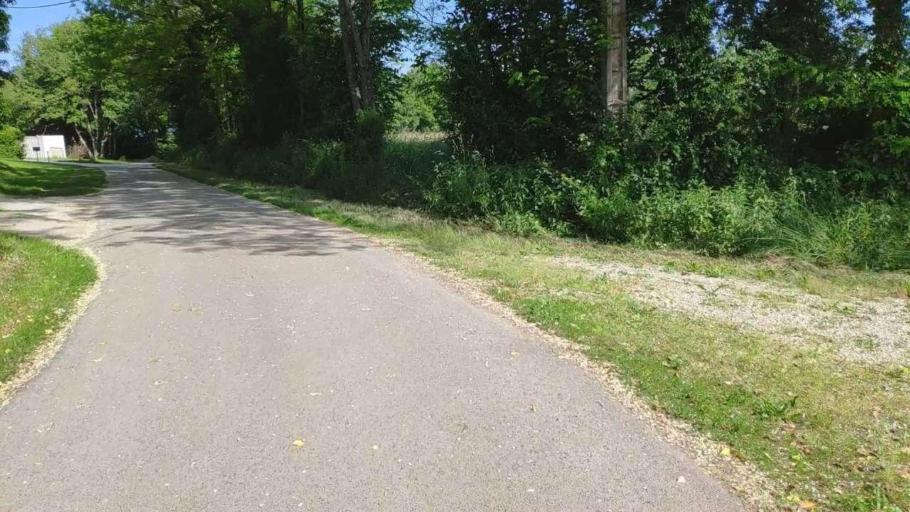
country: FR
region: Franche-Comte
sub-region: Departement du Jura
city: Bletterans
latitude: 46.7144
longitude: 5.4522
